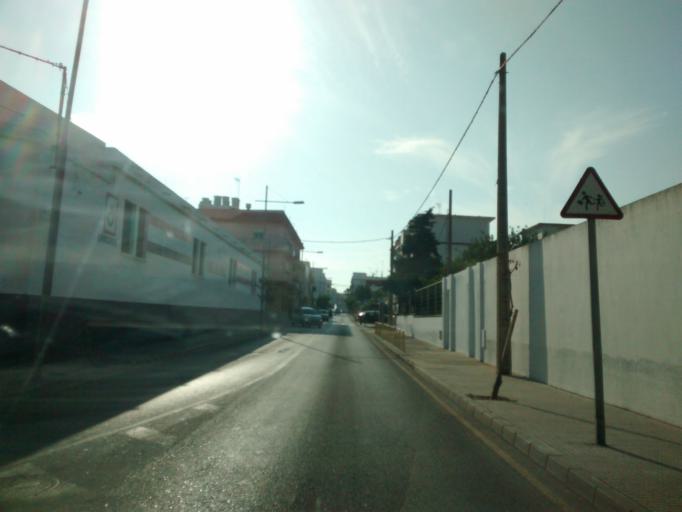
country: ES
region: Andalusia
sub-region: Provincia de Cadiz
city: Barbate de Franco
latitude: 36.1947
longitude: -5.9140
